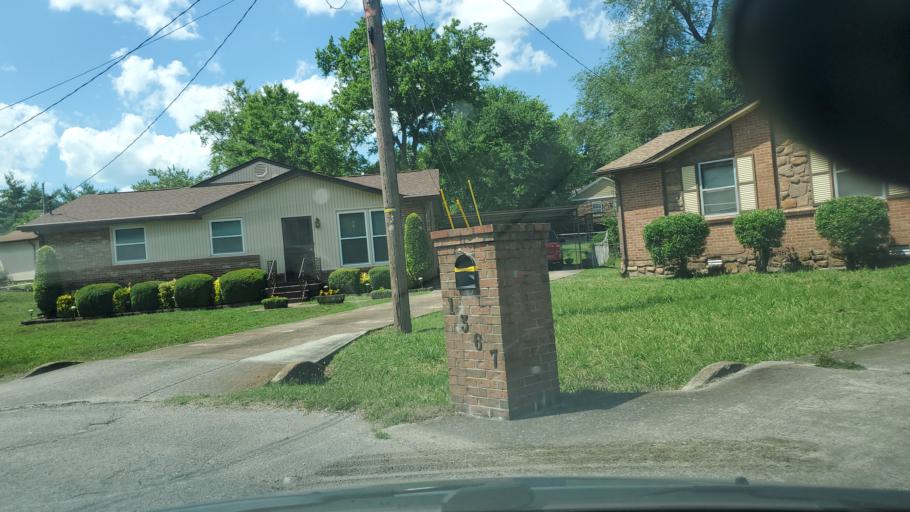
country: US
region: Tennessee
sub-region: Davidson County
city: Nashville
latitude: 36.1951
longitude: -86.7583
